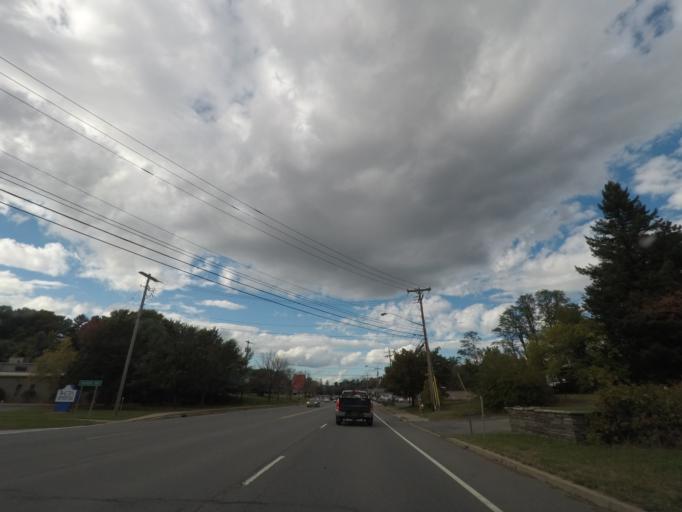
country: US
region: New York
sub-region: Albany County
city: Voorheesville
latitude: 42.7109
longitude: -73.9263
